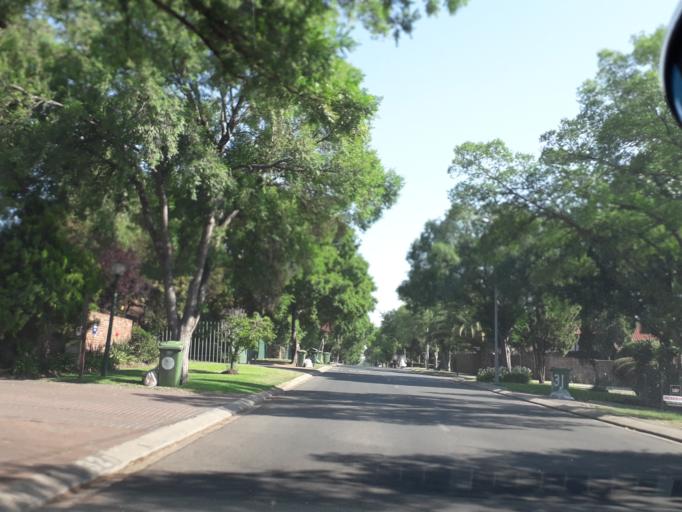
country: ZA
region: Gauteng
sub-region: City of Johannesburg Metropolitan Municipality
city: Midrand
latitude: -26.0341
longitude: 28.0581
